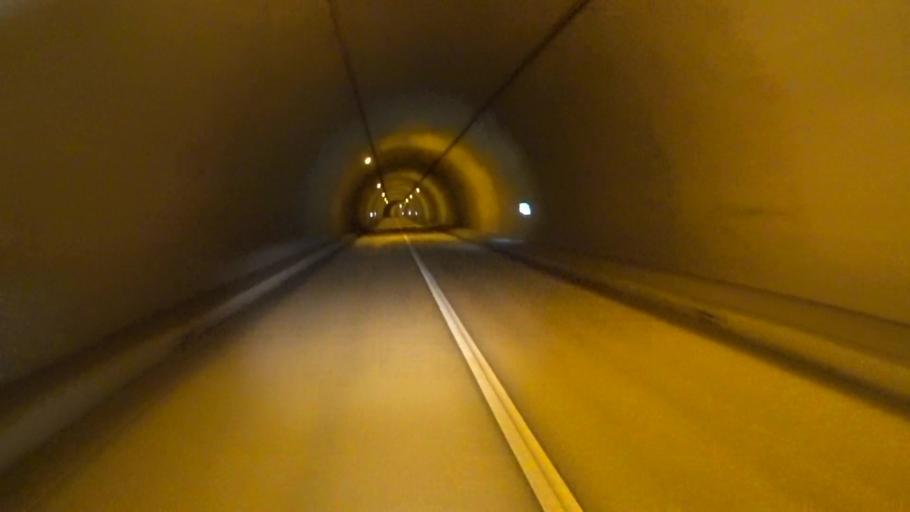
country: JP
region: Hyogo
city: Toyooka
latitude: 35.5281
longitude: 134.9827
